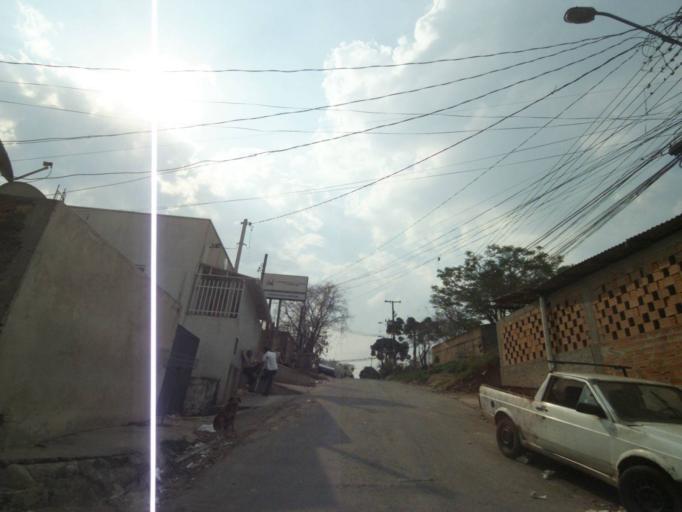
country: BR
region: Parana
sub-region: Curitiba
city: Curitiba
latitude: -25.4631
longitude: -49.2683
